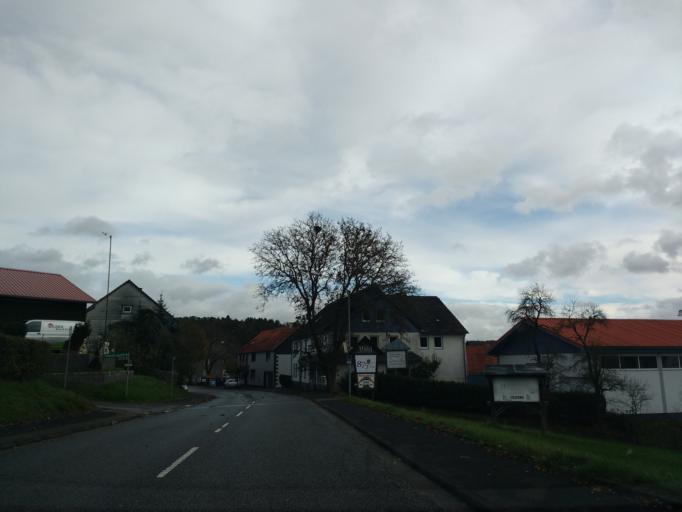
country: DE
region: Hesse
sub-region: Regierungsbezirk Kassel
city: Vohl
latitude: 51.2040
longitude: 8.9394
